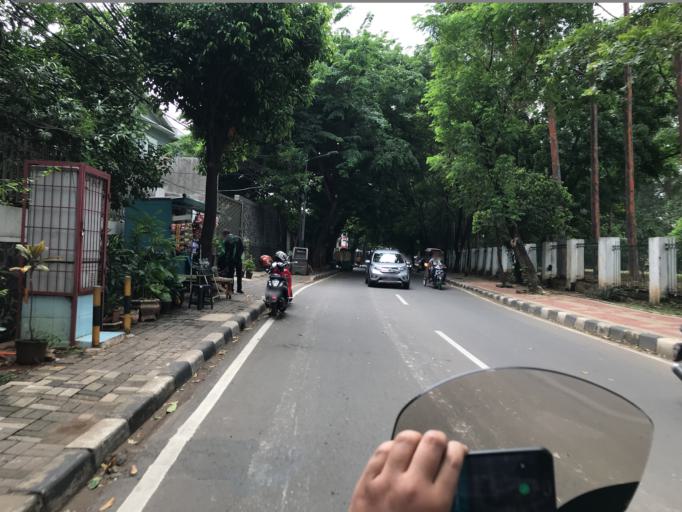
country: ID
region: Jakarta Raya
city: Jakarta
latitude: -6.2358
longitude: 106.8536
